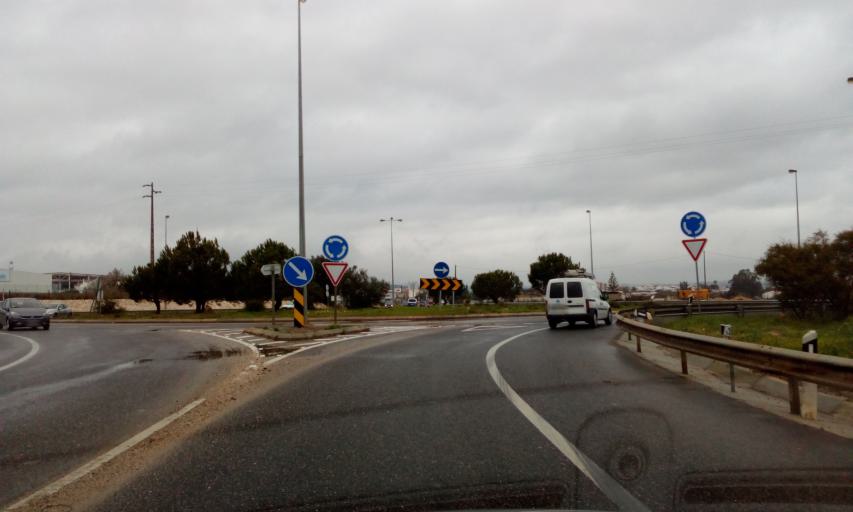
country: PT
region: Faro
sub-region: Lagos
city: Lagos
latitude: 37.1389
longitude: -8.6630
